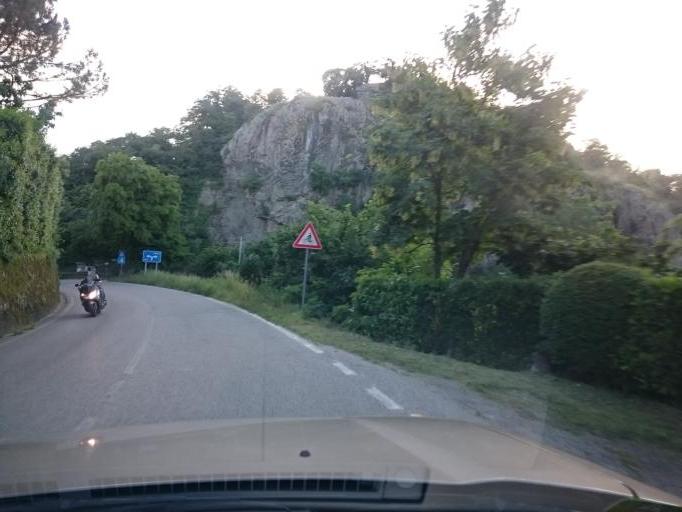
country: IT
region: Veneto
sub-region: Provincia di Padova
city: Treponti
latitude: 45.3315
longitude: 11.6871
